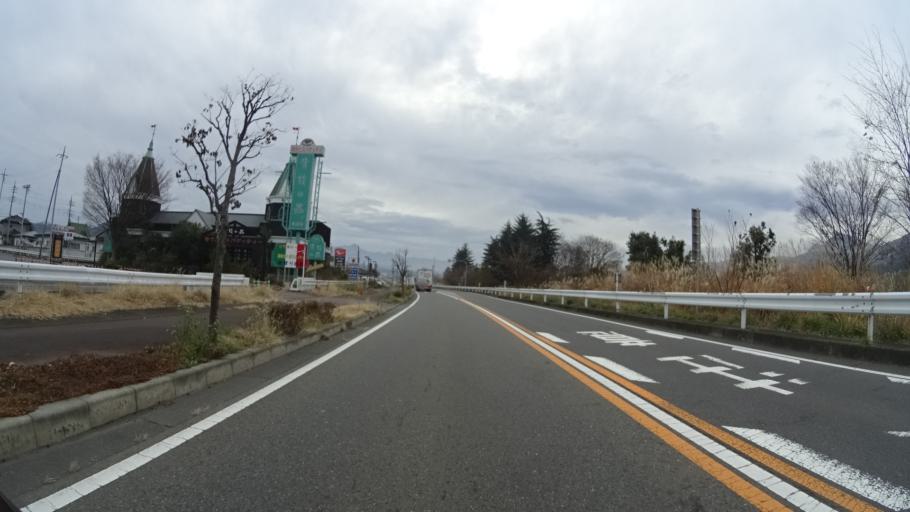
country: JP
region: Gunma
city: Numata
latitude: 36.6510
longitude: 139.0234
